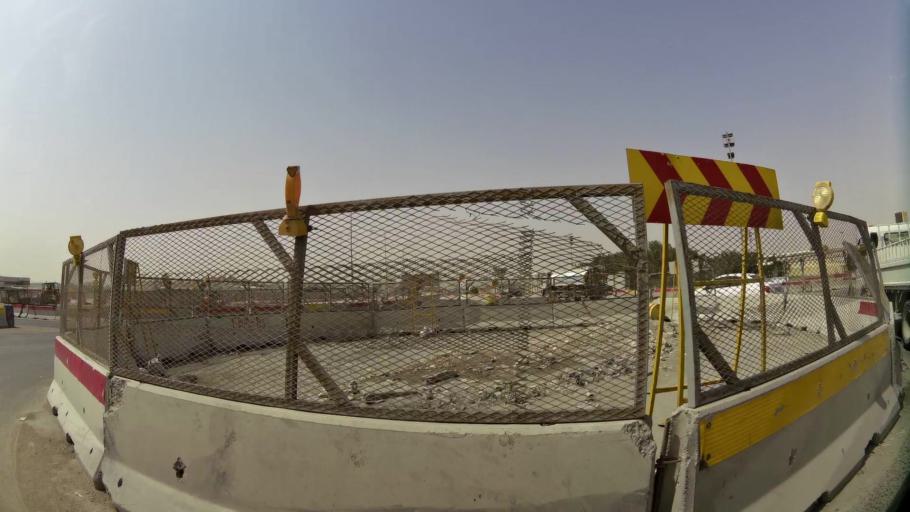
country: QA
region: Baladiyat ar Rayyan
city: Ar Rayyan
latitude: 25.2126
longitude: 51.4197
